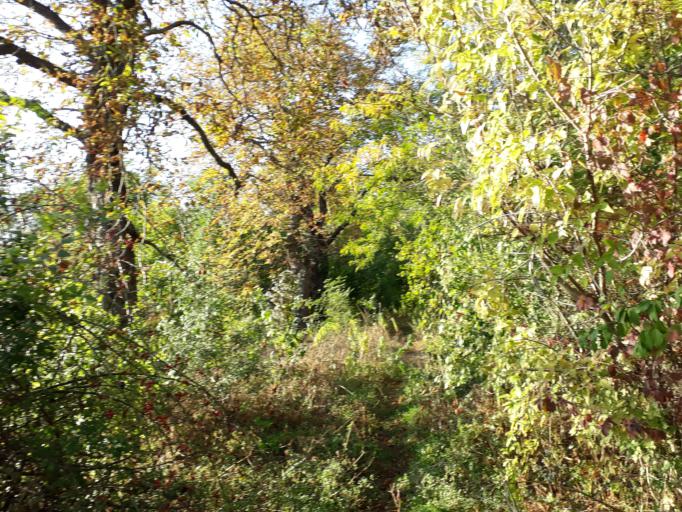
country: HU
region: Budapest
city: Budapest XI. keruelet
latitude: 47.4556
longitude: 19.0054
